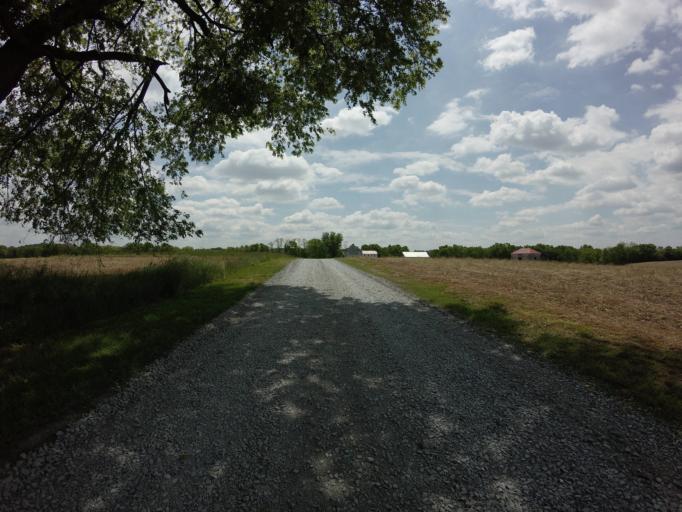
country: US
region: Maryland
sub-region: Frederick County
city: Ballenger Creek
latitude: 39.3723
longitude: -77.3987
